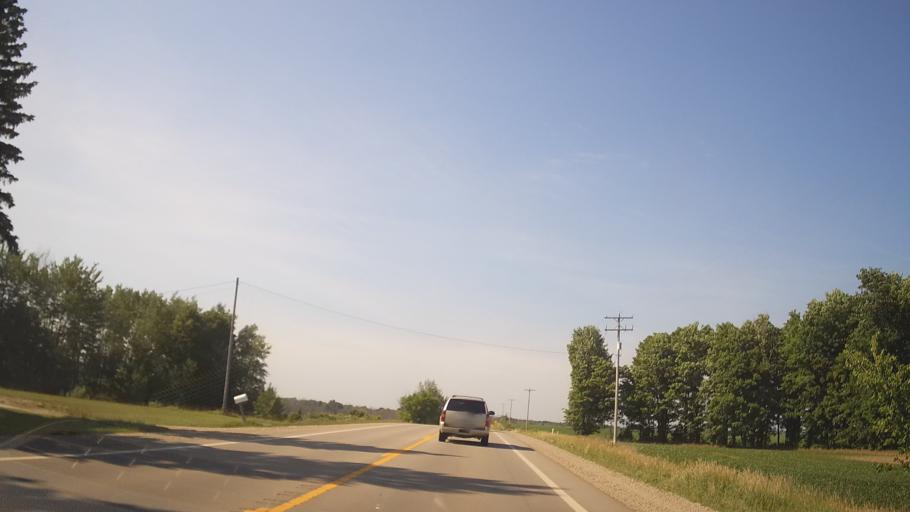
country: US
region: Michigan
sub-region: Ogemaw County
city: West Branch
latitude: 44.3154
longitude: -84.1257
